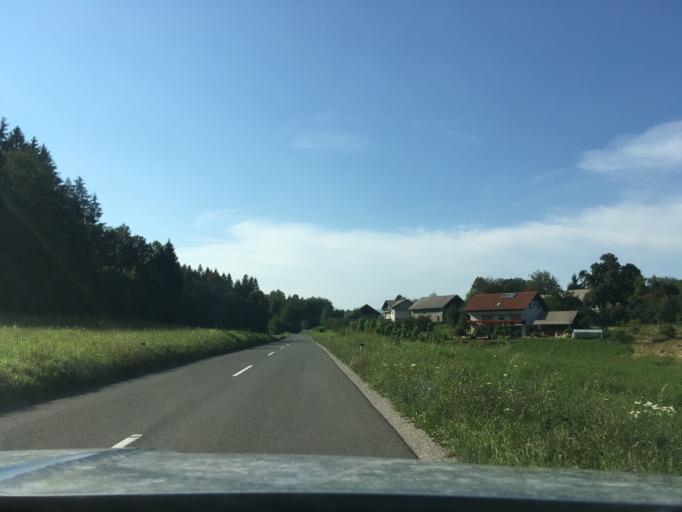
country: SI
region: Crnomelj
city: Crnomelj
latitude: 45.5062
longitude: 15.1890
